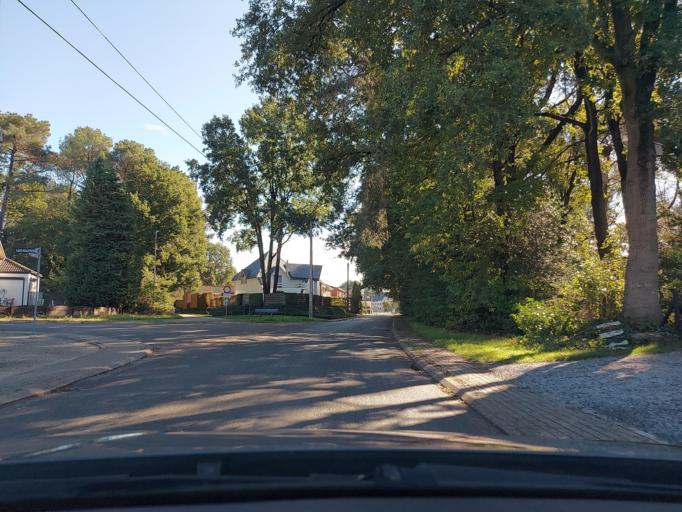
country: BE
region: Flanders
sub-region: Provincie Limburg
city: Houthalen
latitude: 51.0301
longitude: 5.3599
